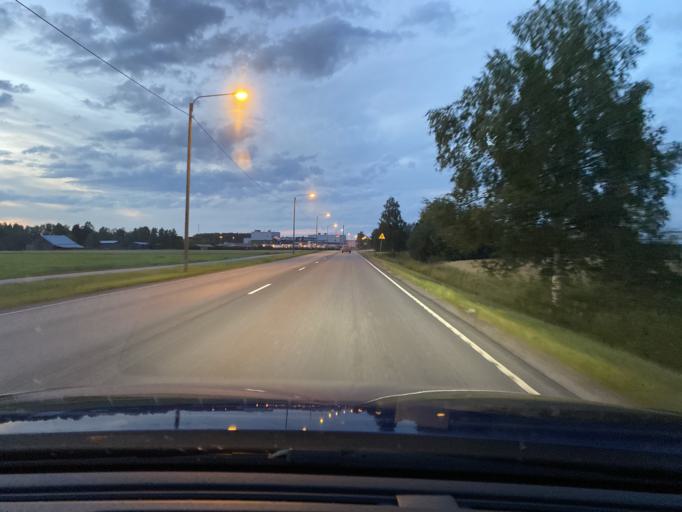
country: FI
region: Southern Ostrobothnia
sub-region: Suupohja
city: Kauhajoki
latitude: 62.4406
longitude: 22.2093
